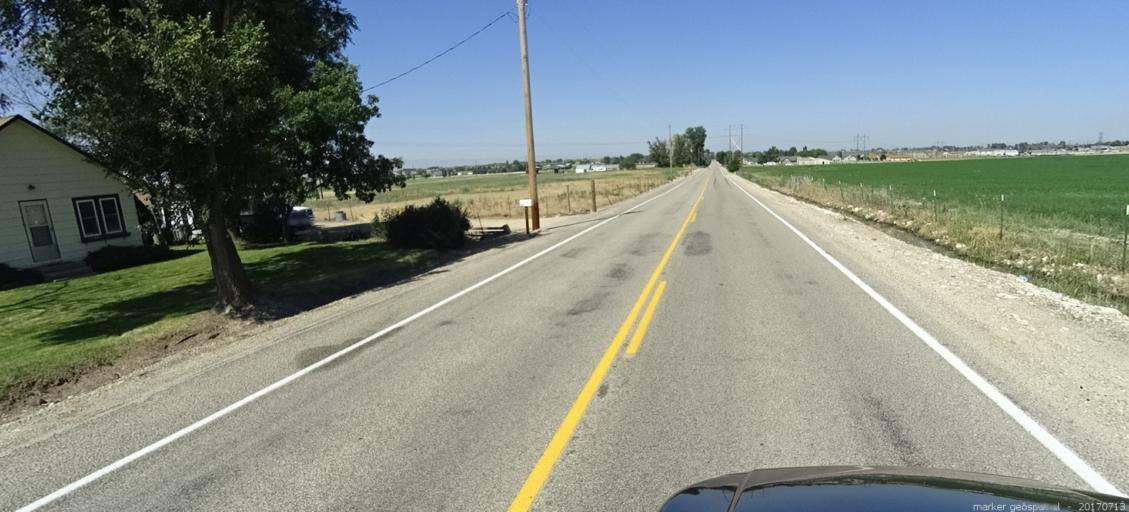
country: US
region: Idaho
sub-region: Ada County
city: Kuna
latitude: 43.5319
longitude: -116.3799
